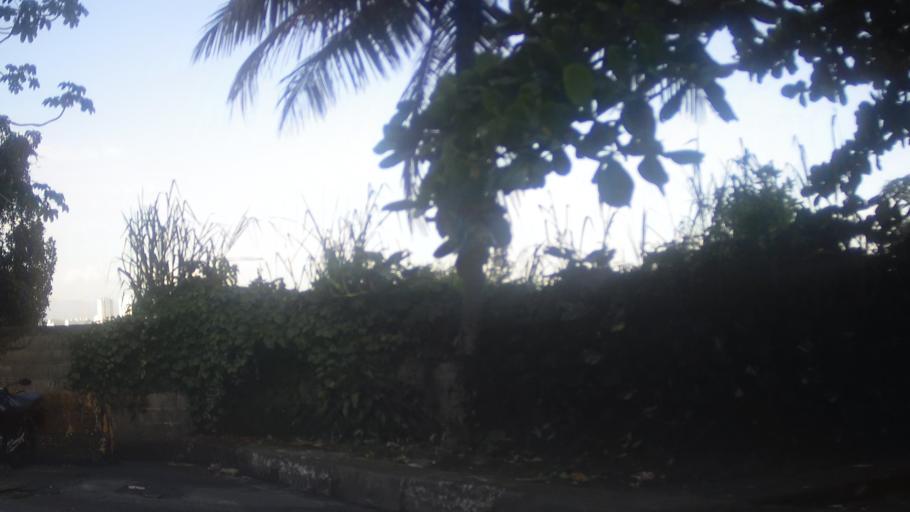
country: BR
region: Sao Paulo
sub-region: Sao Vicente
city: Sao Vicente
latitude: -23.9812
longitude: -46.3682
